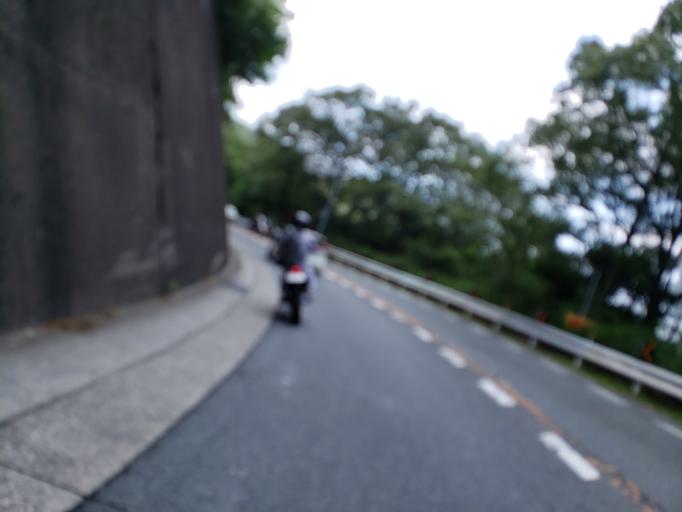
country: JP
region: Hyogo
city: Aioi
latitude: 34.7811
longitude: 134.4362
